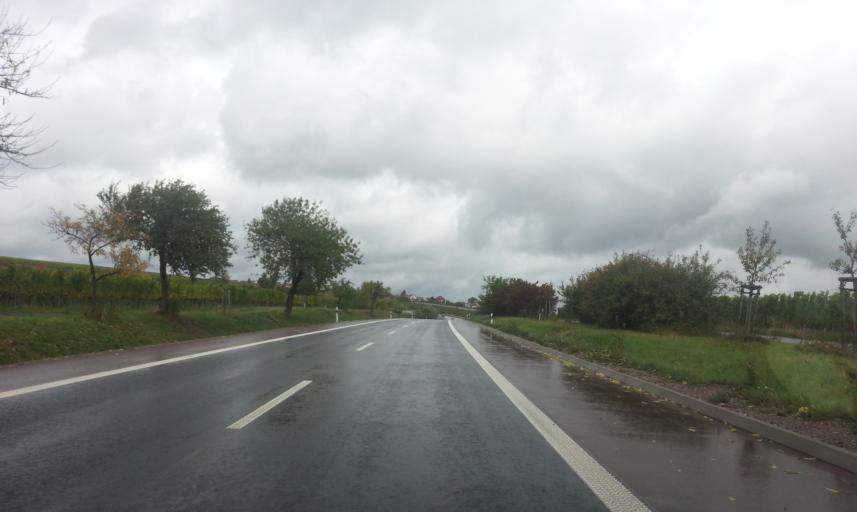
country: DE
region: Rheinland-Pfalz
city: Kallstadt
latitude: 49.4989
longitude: 8.1759
